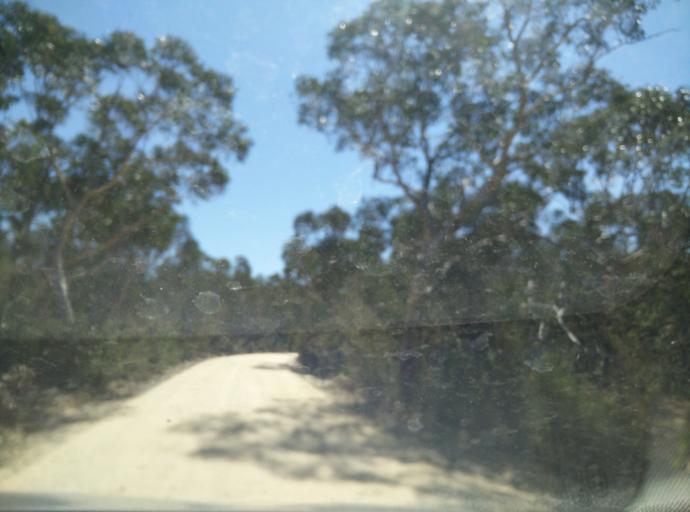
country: AU
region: New South Wales
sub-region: Blue Mountains Municipality
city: Blackheath
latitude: -33.5808
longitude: 150.2747
